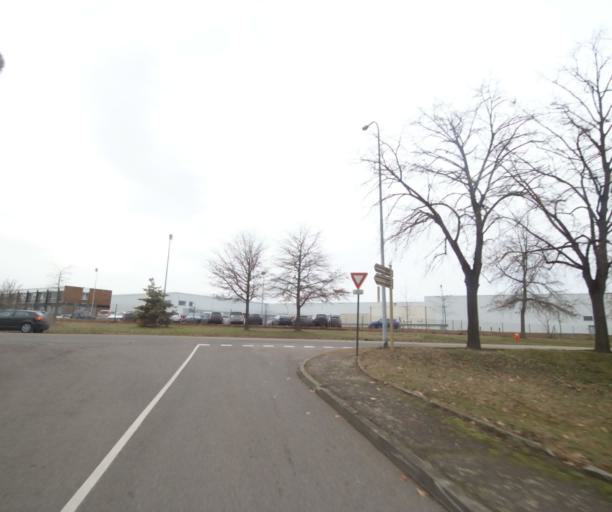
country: FR
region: Rhone-Alpes
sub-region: Departement de la Loire
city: Le Coteau
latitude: 46.0608
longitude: 4.0913
